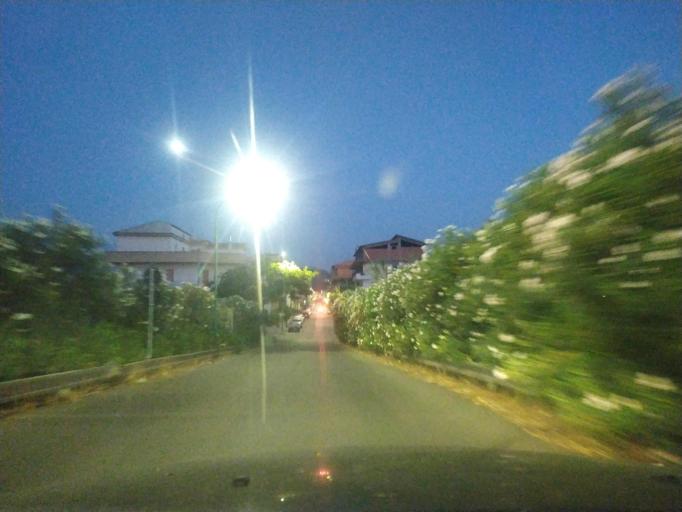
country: IT
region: Sicily
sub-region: Messina
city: Terme
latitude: 38.1406
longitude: 15.1609
